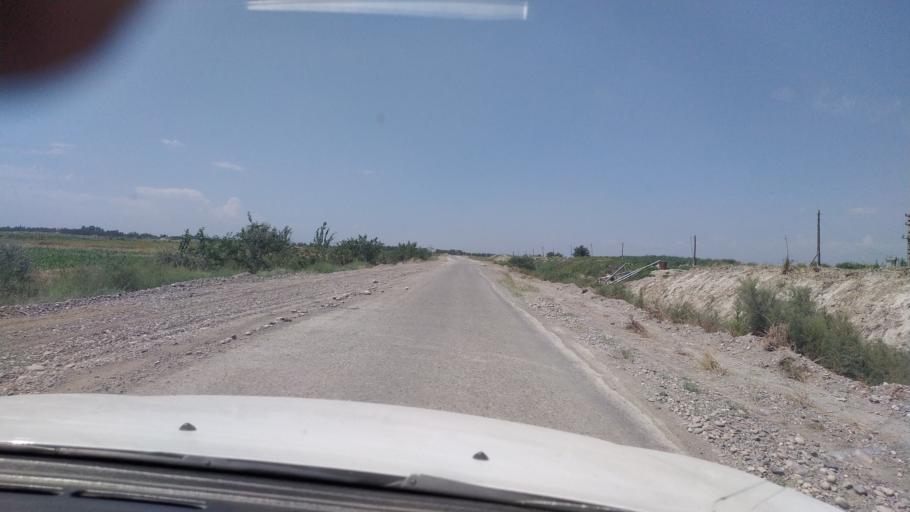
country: UZ
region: Namangan
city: Toshbuloq
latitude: 40.7927
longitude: 71.5746
